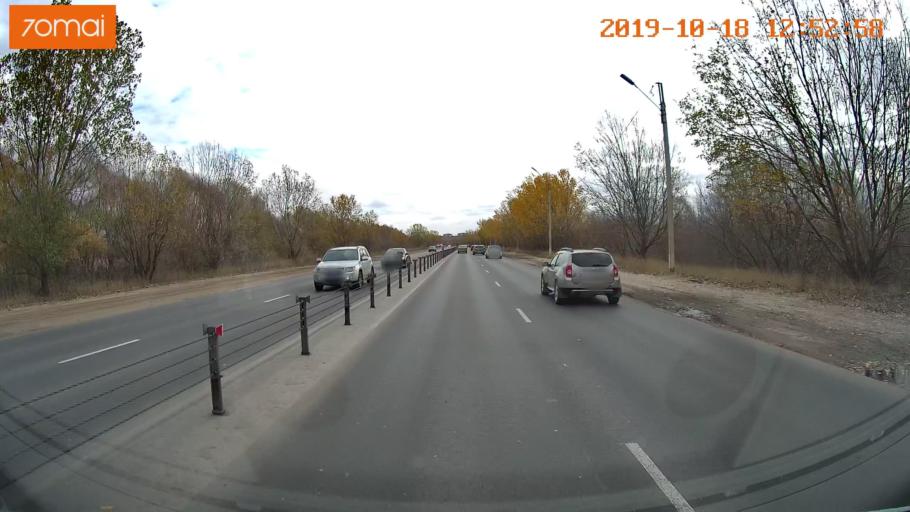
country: RU
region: Rjazan
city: Ryazan'
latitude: 54.6481
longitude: 39.7003
